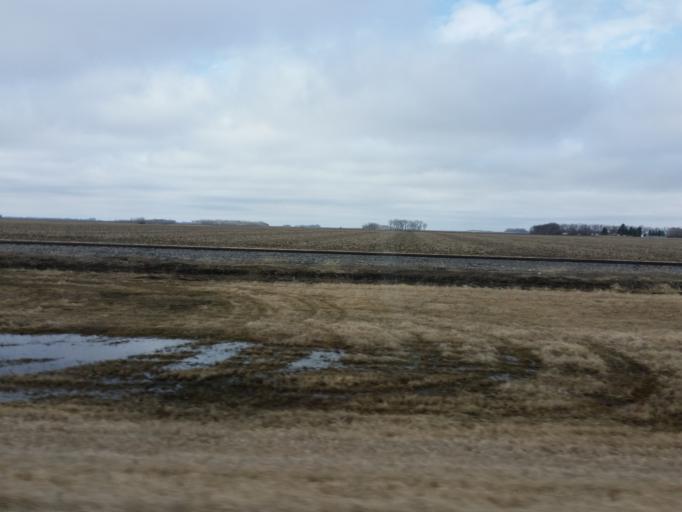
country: US
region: North Dakota
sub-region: Cass County
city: Casselton
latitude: 47.0441
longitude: -97.2181
